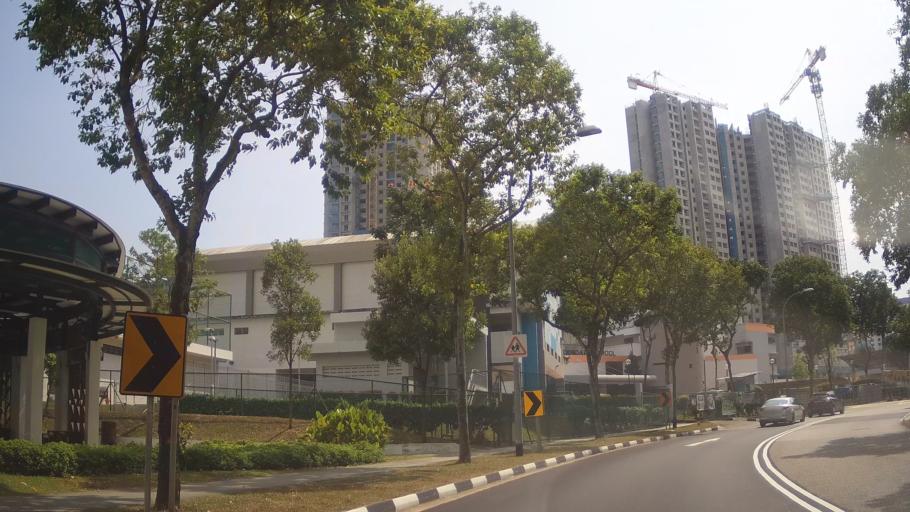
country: MY
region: Johor
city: Johor Bahru
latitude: 1.3870
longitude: 103.7588
